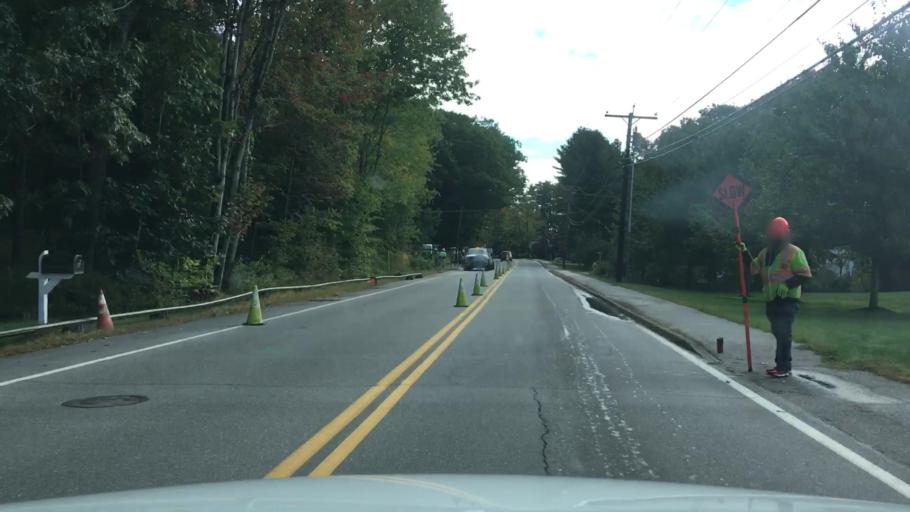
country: US
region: Maine
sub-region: Cumberland County
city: Brunswick
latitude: 43.9246
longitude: -69.9472
